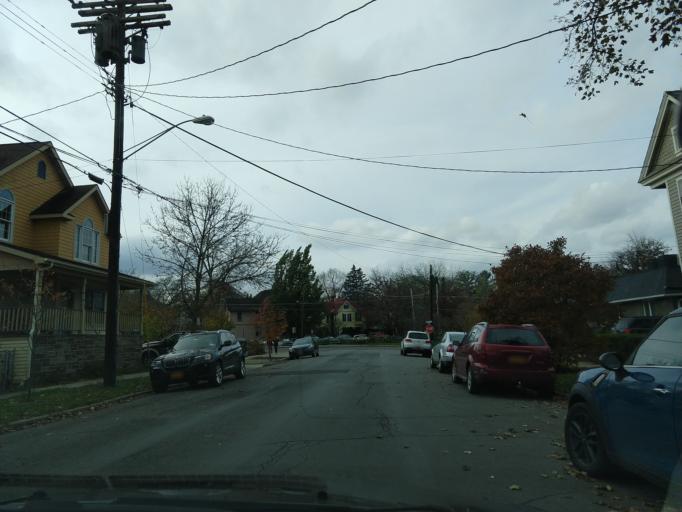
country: US
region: New York
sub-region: Tompkins County
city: Ithaca
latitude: 42.4450
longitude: -76.4985
